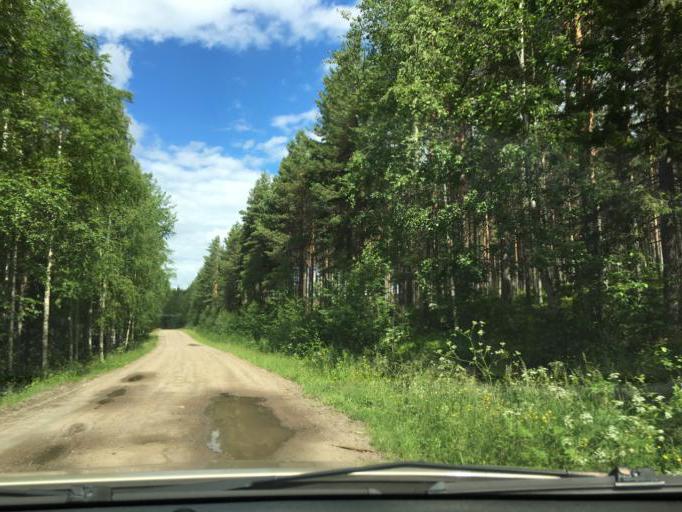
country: SE
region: Norrbotten
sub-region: Overkalix Kommun
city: OEverkalix
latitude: 66.1295
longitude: 22.7846
